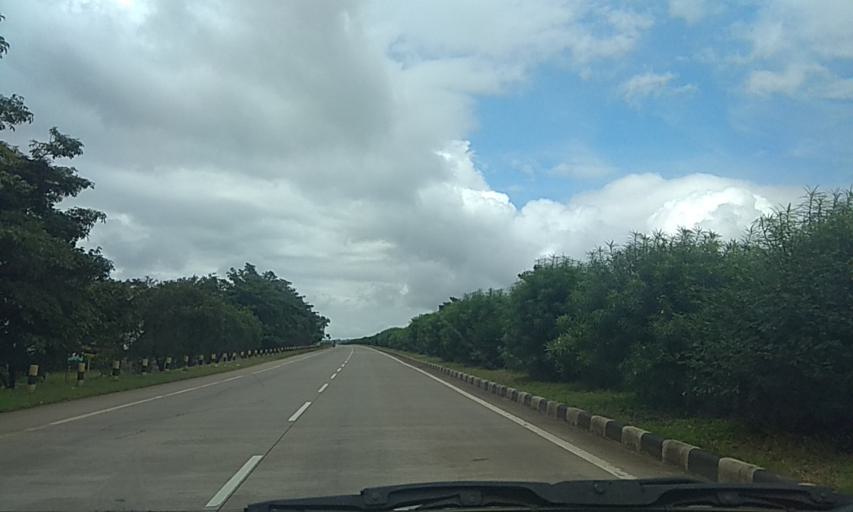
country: IN
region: Karnataka
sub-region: Belgaum
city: Sankeshwar
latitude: 16.3087
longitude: 74.4307
